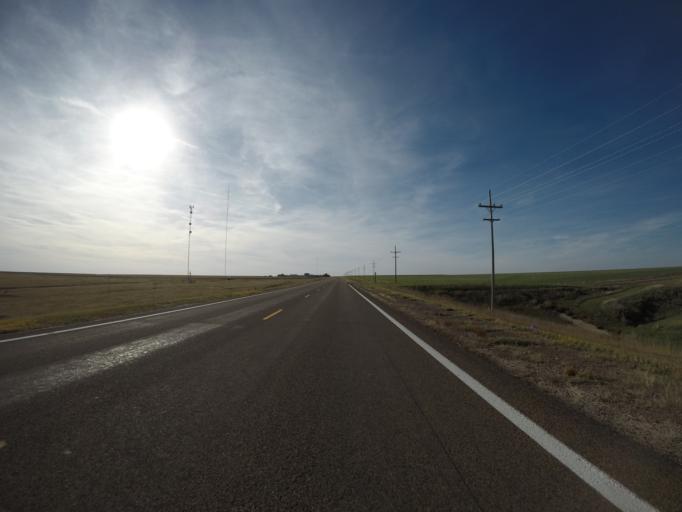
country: US
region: Kansas
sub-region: Rawlins County
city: Atwood
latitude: 39.7854
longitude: -101.2598
